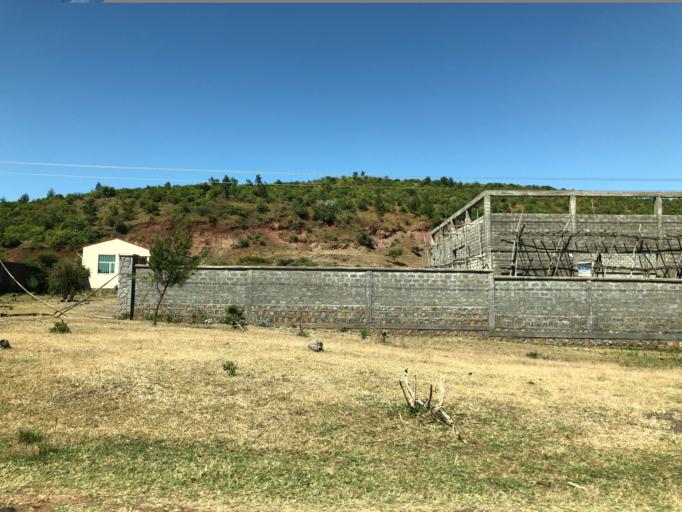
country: ET
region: Amhara
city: Adis Zemen
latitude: 12.1026
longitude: 37.7621
